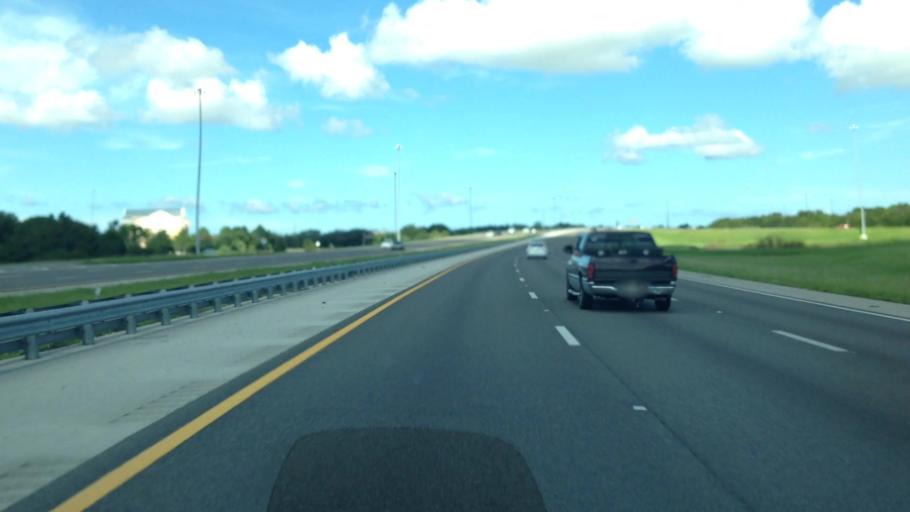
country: US
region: Florida
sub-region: Sarasota County
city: Plantation
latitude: 27.1098
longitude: -82.3787
